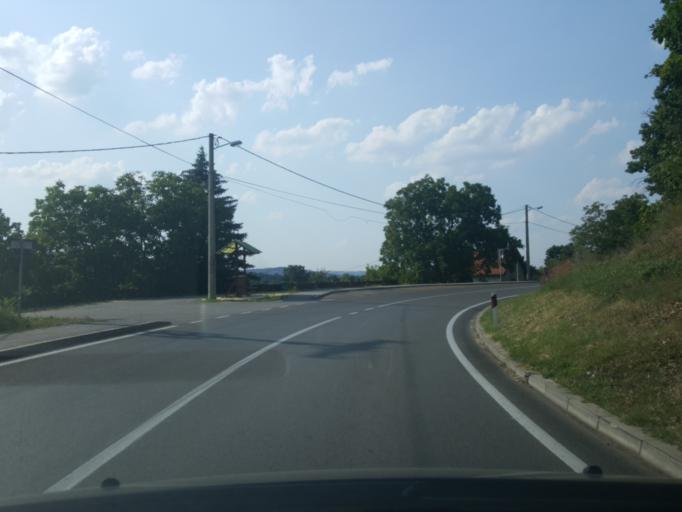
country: RS
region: Central Serbia
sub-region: Sumadijski Okrug
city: Topola
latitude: 44.2408
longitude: 20.6770
